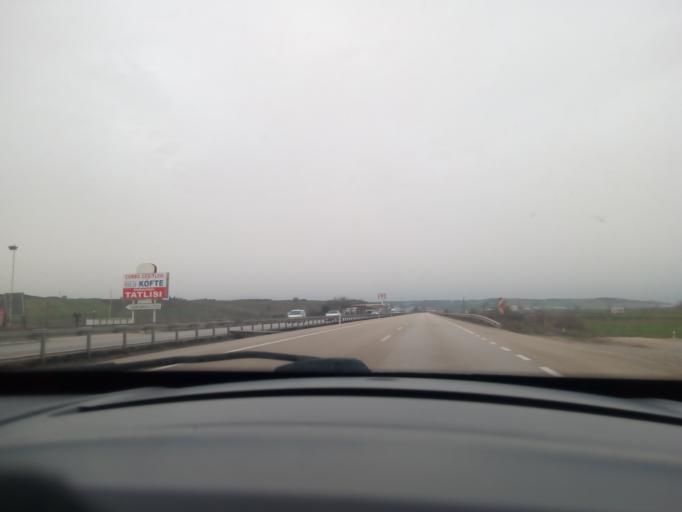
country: TR
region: Bursa
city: Tatkavakli
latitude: 40.0294
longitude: 28.3048
